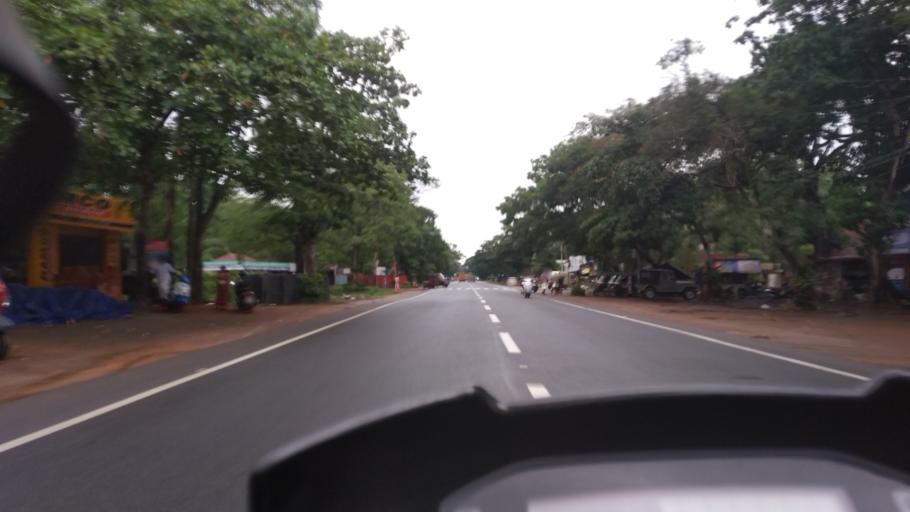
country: IN
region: Kerala
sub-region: Alappuzha
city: Mavelikara
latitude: 9.3100
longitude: 76.4309
